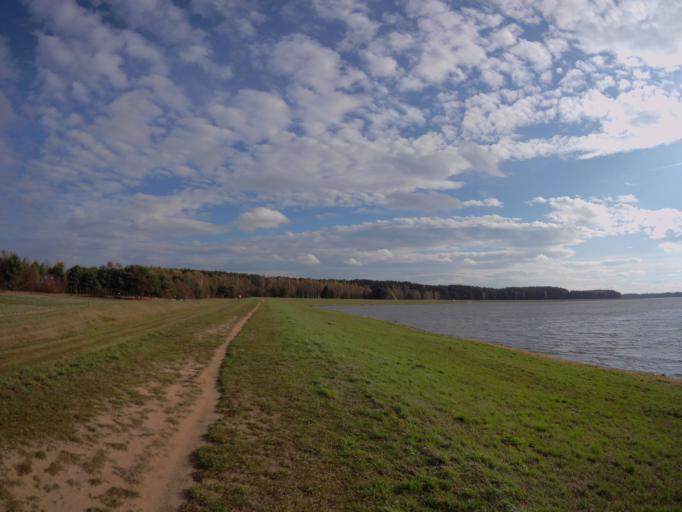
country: PL
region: Subcarpathian Voivodeship
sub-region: Powiat kolbuszowski
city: Lipnica
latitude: 50.3389
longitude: 21.9389
